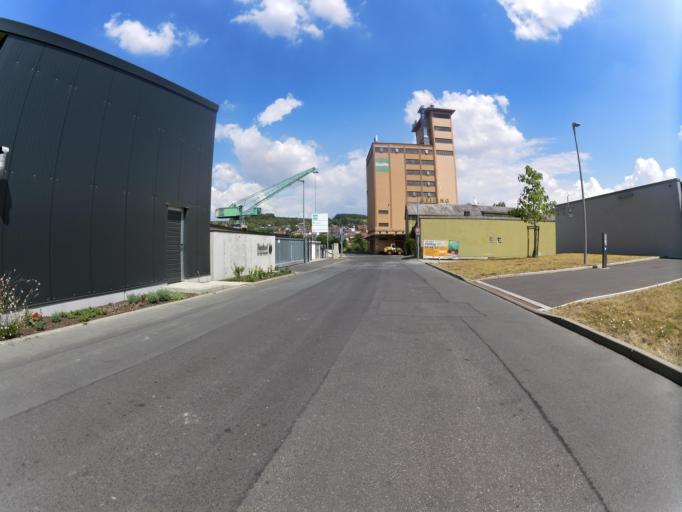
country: DE
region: Bavaria
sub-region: Regierungsbezirk Unterfranken
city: Ochsenfurt
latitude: 49.6666
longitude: 10.0538
